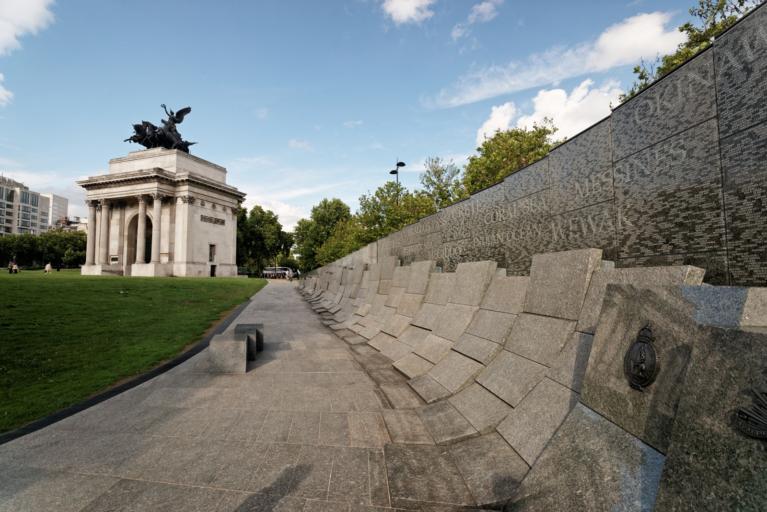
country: GB
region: England
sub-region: Greater London
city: Chelsea
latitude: 51.5021
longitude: -0.1514
